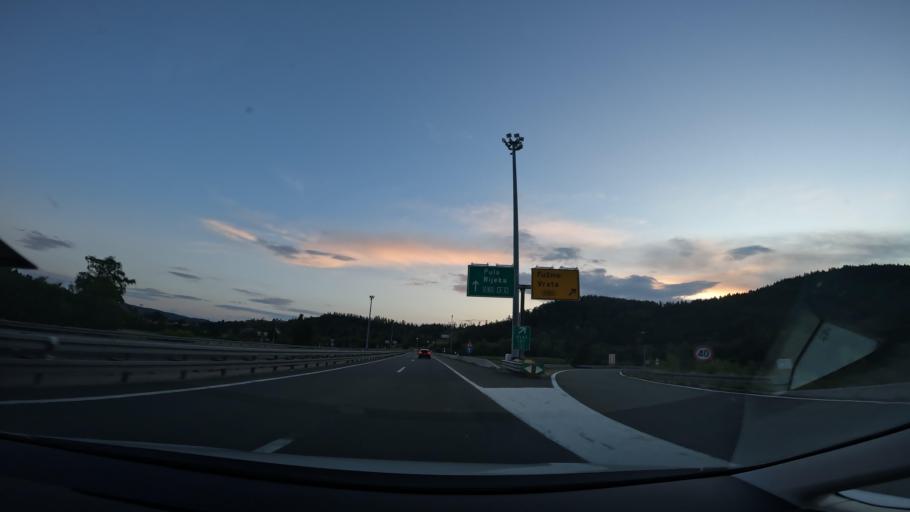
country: HR
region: Primorsko-Goranska
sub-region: Grad Delnice
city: Delnice
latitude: 45.3201
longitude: 14.7279
